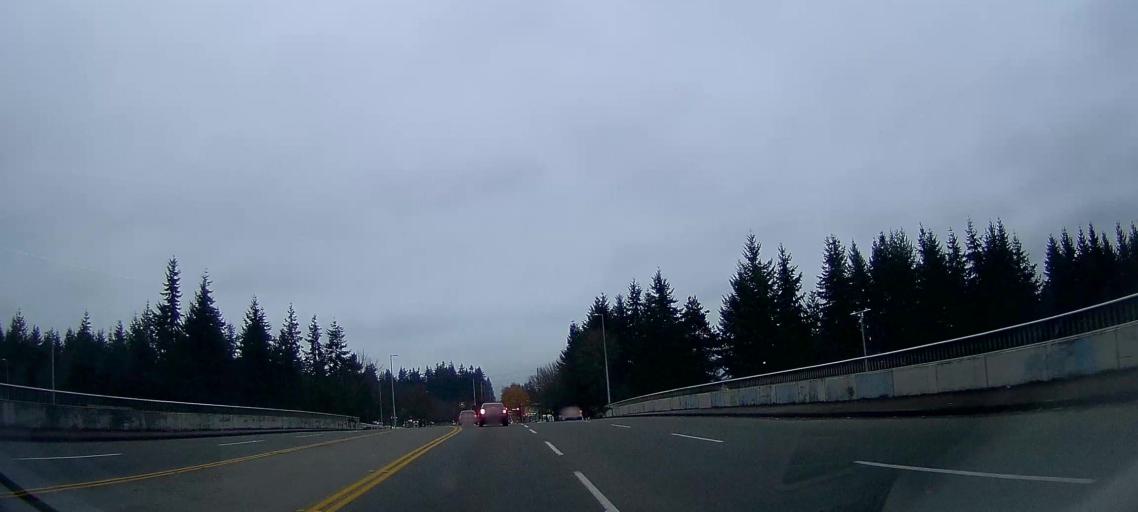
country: US
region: Washington
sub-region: Thurston County
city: Lacey
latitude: 47.0454
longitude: -122.8337
